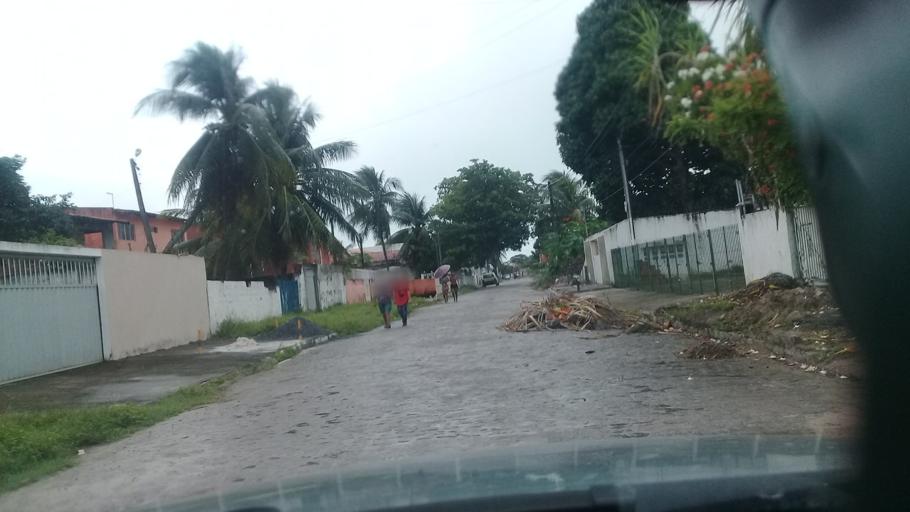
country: BR
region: Pernambuco
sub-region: Itamaraca
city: Itamaraca
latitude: -7.7533
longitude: -34.8262
